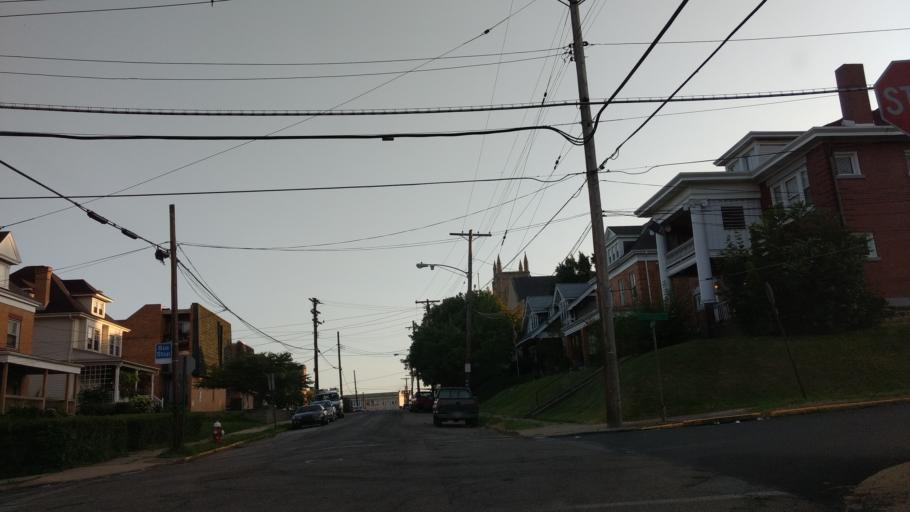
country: US
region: Pennsylvania
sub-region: Allegheny County
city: Bellevue
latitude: 40.4960
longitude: -80.0517
